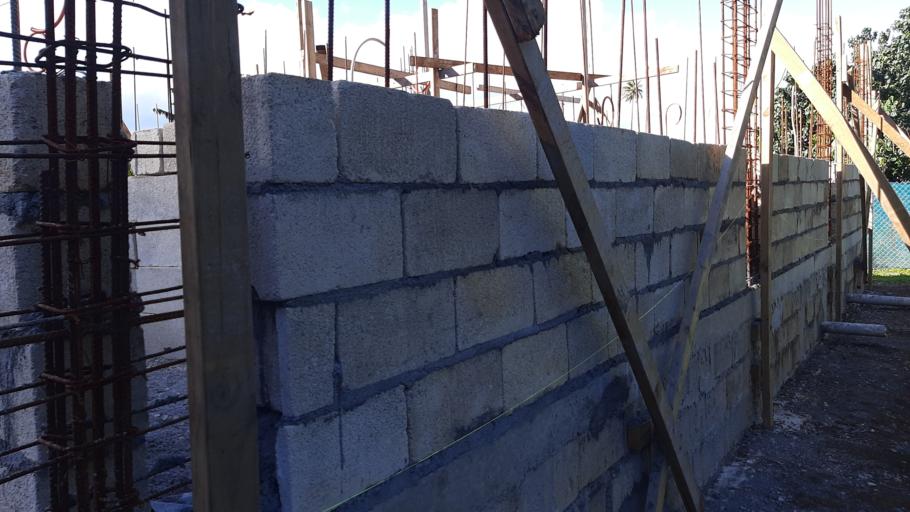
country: VU
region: Tafea
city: Isangel
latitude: -18.7461
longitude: 169.2033
